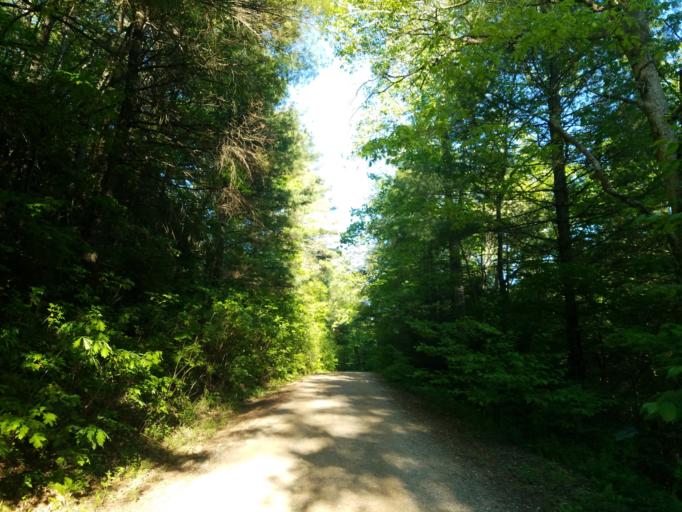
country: US
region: Georgia
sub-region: Lumpkin County
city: Dahlonega
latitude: 34.6803
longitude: -84.1359
